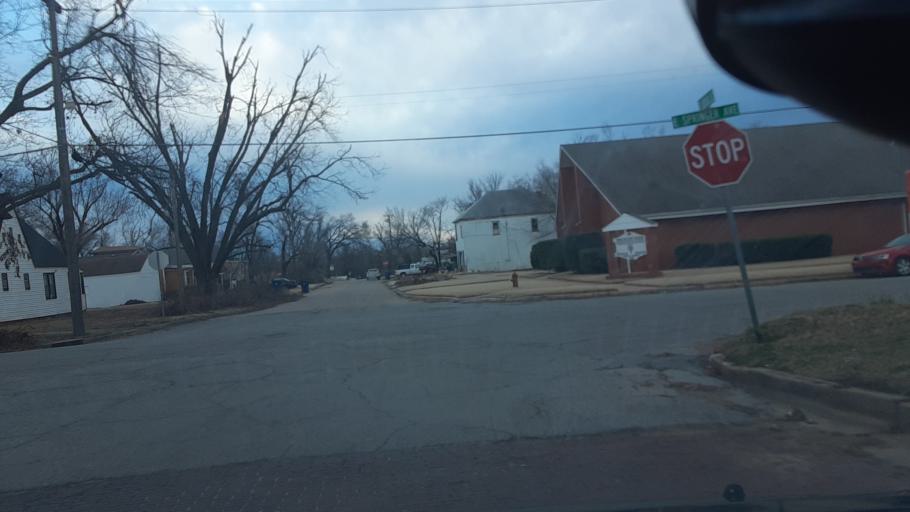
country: US
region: Oklahoma
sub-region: Logan County
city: Guthrie
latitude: 35.8751
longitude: -97.4228
